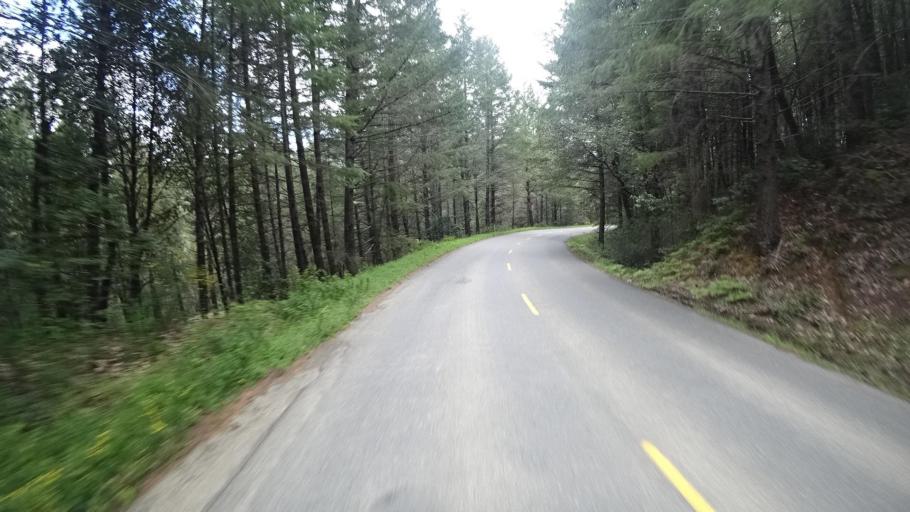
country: US
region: California
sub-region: Humboldt County
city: Redway
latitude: 40.1049
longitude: -123.9253
